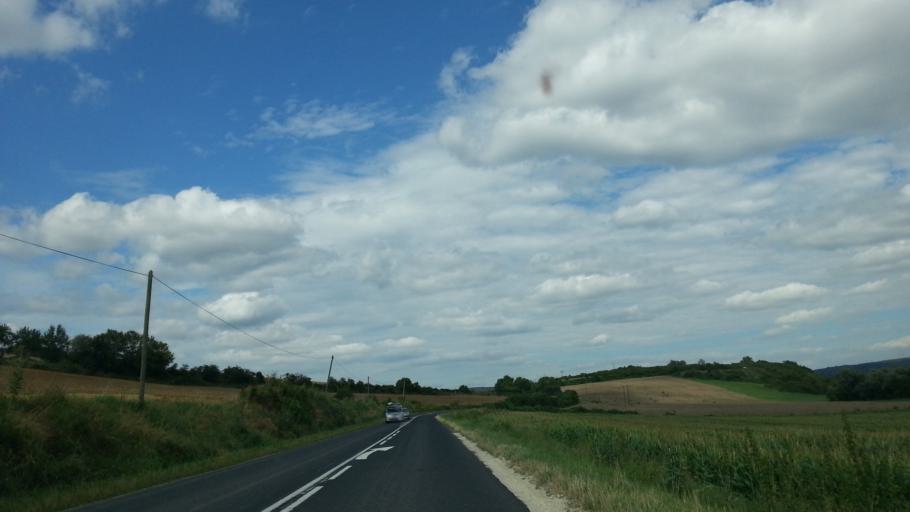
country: FR
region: Lorraine
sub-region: Departement de la Meuse
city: Thierville-sur-Meuse
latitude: 49.1957
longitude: 5.3432
